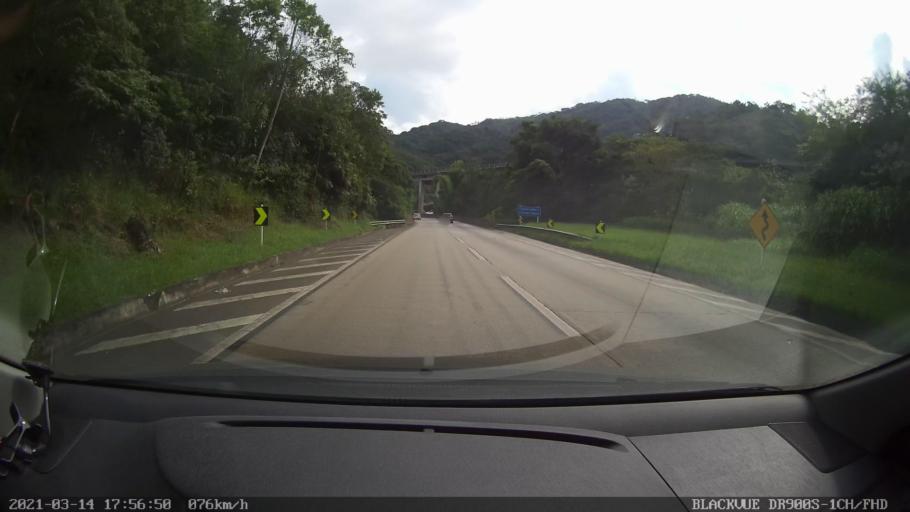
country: BR
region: Rio de Janeiro
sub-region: Petropolis
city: Petropolis
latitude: -22.5117
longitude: -43.2305
